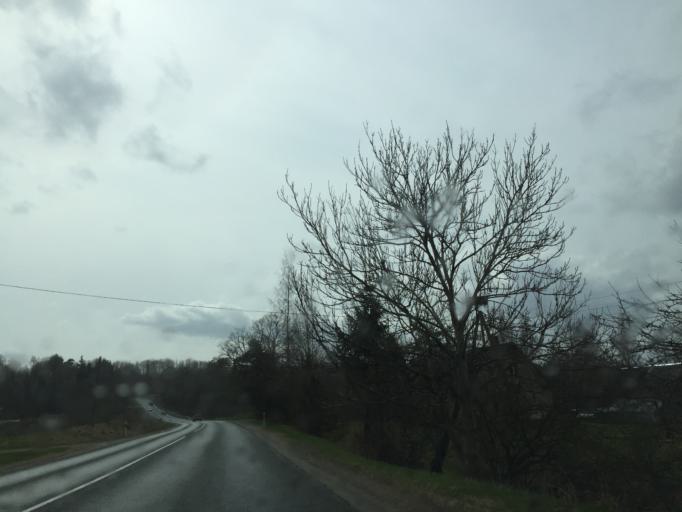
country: LV
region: Priekuli
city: Priekuli
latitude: 57.3374
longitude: 25.3310
